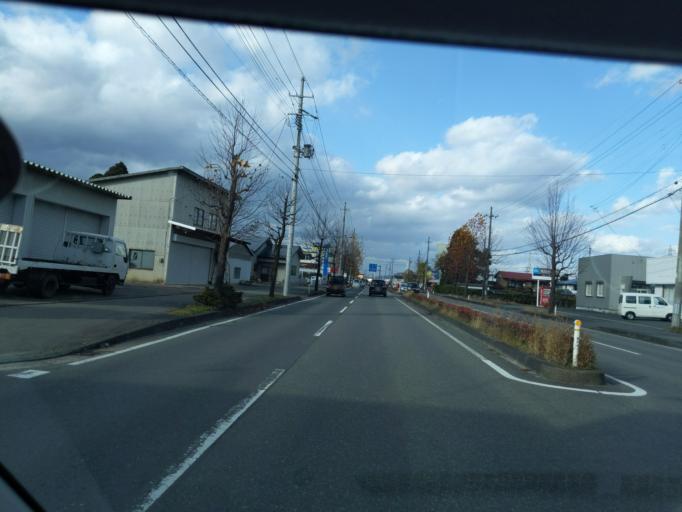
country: JP
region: Iwate
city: Mizusawa
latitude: 39.1506
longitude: 141.1541
